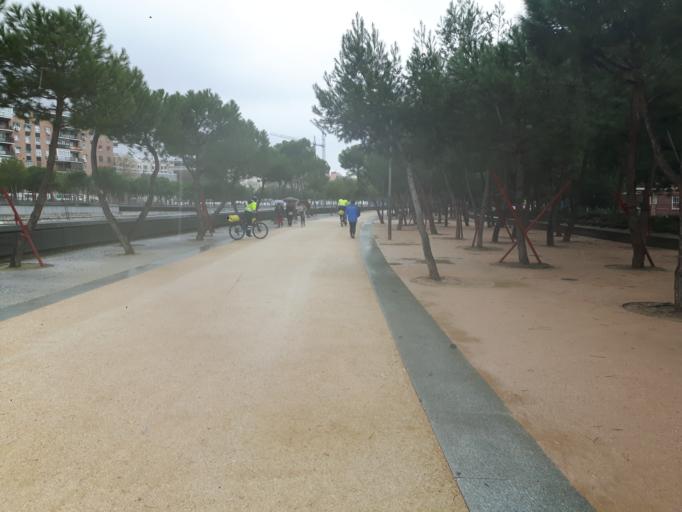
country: ES
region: Madrid
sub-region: Provincia de Madrid
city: Carabanchel
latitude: 40.4098
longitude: -3.7223
